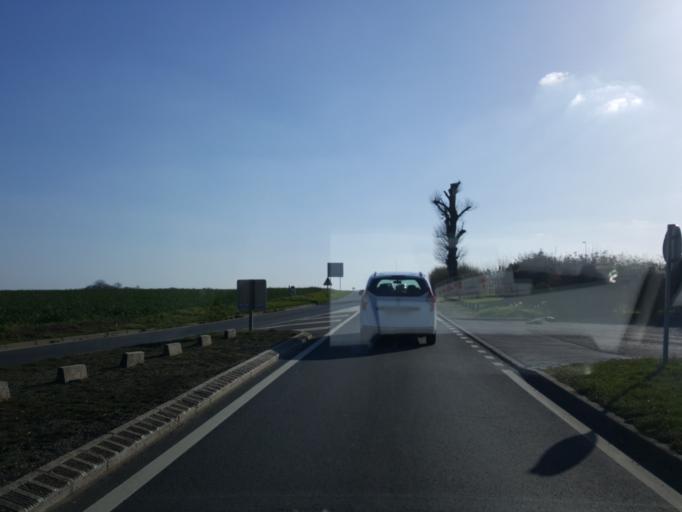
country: FR
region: Ile-de-France
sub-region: Departement des Yvelines
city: Rambouillet
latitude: 48.6229
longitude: 1.8217
